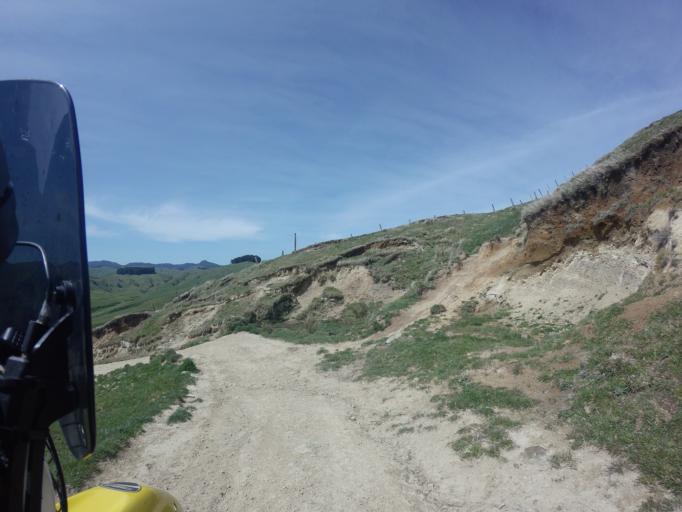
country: NZ
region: Bay of Plenty
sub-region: Opotiki District
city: Opotiki
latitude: -38.4668
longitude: 177.3787
